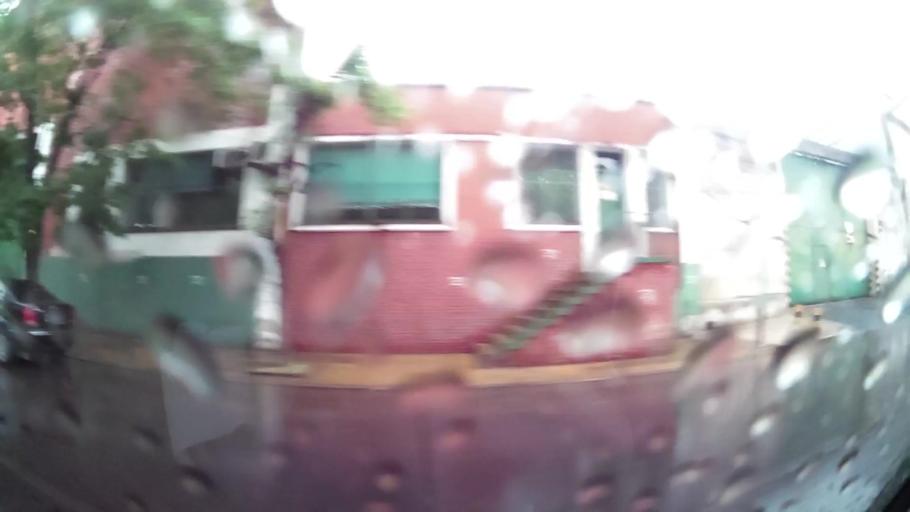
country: AR
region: Buenos Aires
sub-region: Partido de Avellaneda
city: Avellaneda
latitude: -34.6478
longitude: -58.3676
